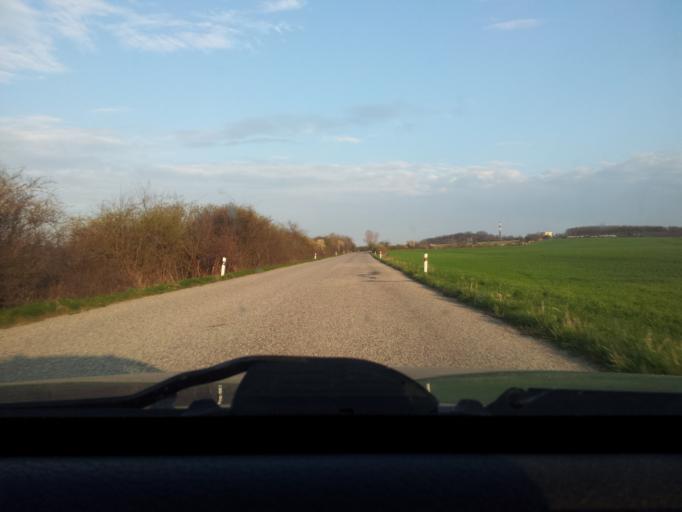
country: SK
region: Nitriansky
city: Tlmace
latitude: 48.2829
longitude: 18.4681
